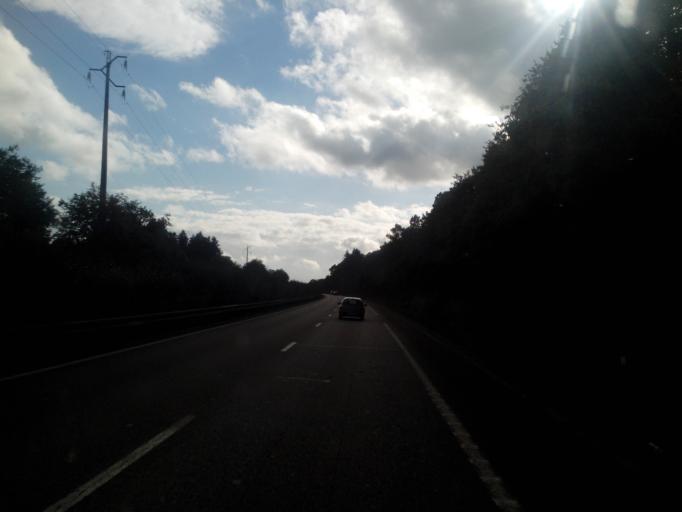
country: FR
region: Brittany
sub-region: Departement du Morbihan
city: Saint-Nolff
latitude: 47.6899
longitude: -2.6420
